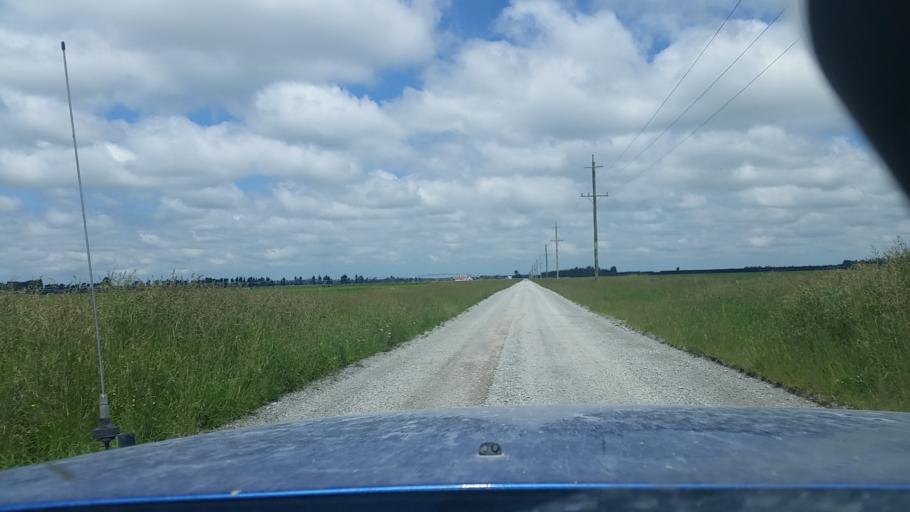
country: NZ
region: Canterbury
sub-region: Ashburton District
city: Tinwald
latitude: -43.8577
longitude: 171.3752
